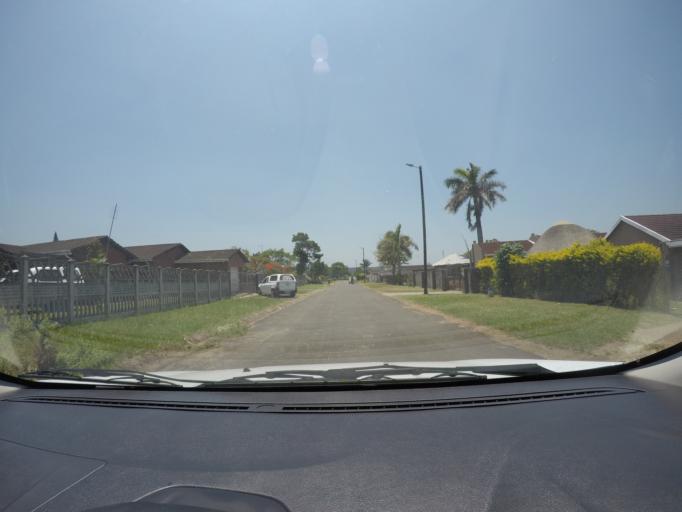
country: ZA
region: KwaZulu-Natal
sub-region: uThungulu District Municipality
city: eSikhawini
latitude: -28.8857
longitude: 31.8944
